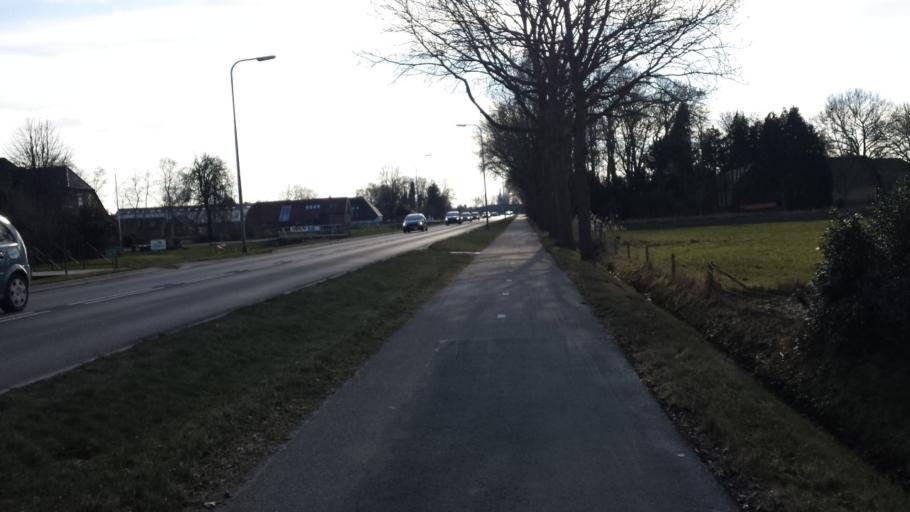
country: NL
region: Overijssel
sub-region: Gemeente Steenwijkerland
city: Steenwijk
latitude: 52.8078
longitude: 6.1311
